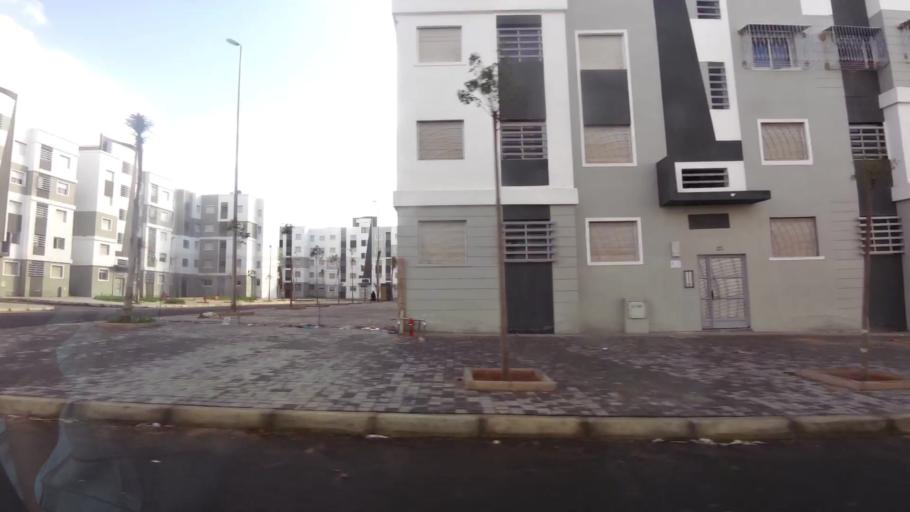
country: MA
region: Grand Casablanca
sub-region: Casablanca
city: Casablanca
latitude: 33.5529
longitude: -7.7047
